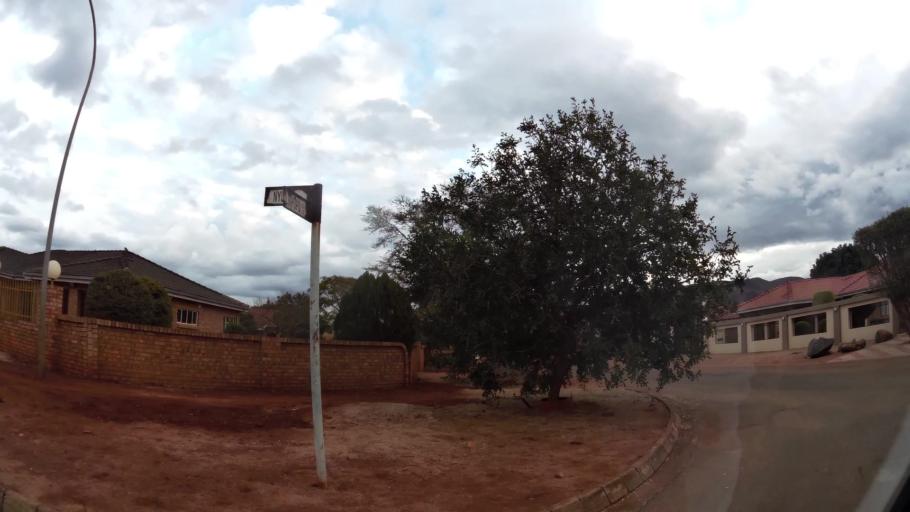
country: ZA
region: Limpopo
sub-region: Waterberg District Municipality
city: Mokopane
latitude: -24.1992
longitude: 28.9884
